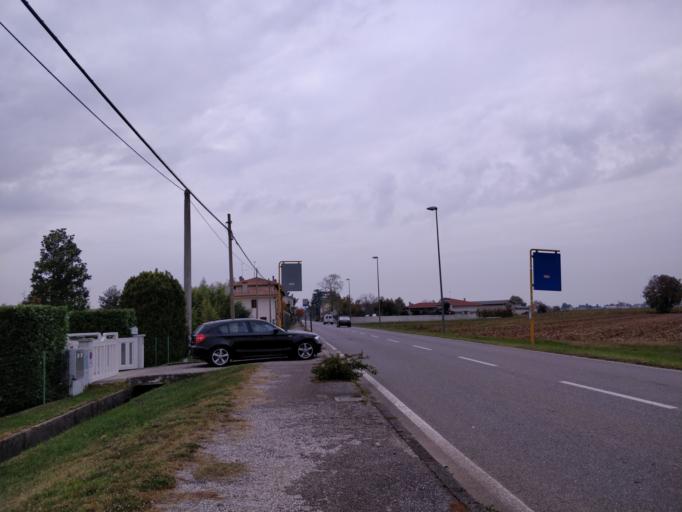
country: IT
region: Friuli Venezia Giulia
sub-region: Provincia di Udine
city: Bertiolo
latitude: 45.9401
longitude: 13.0647
